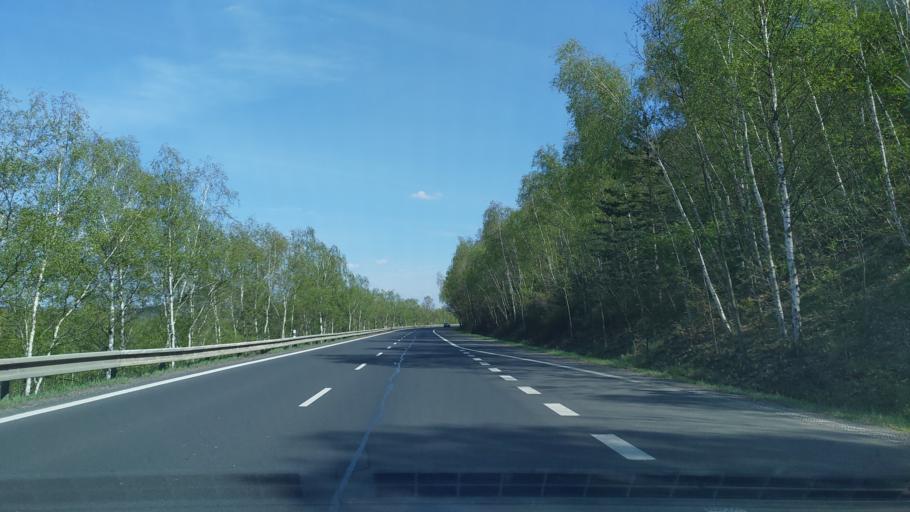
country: CZ
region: Ustecky
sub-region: Okres Most
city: Most
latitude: 50.5241
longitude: 13.6330
